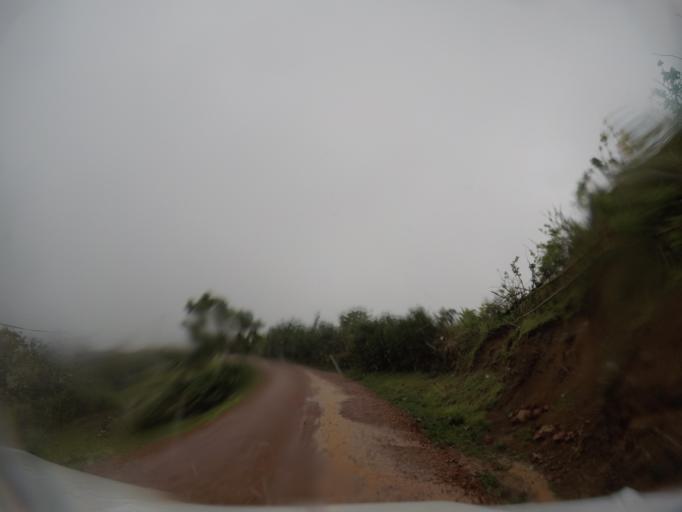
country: TL
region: Baucau
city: Venilale
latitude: -8.6389
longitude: 126.4074
